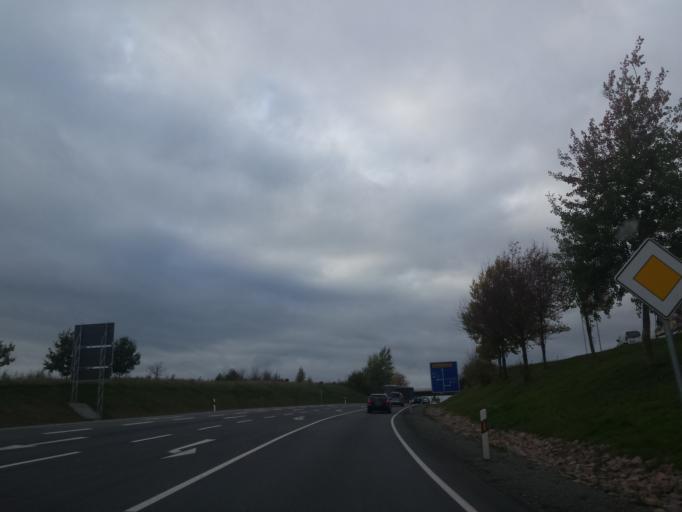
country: DE
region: Saxony
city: Stollberg
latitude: 50.7018
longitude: 12.7588
